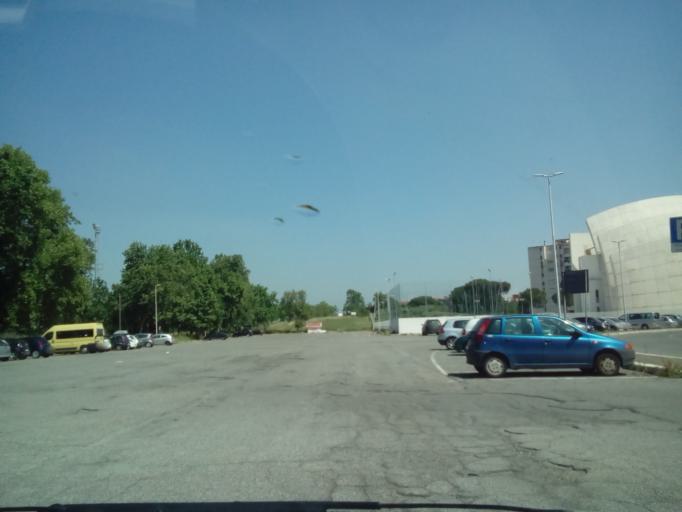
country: IT
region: Latium
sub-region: Citta metropolitana di Roma Capitale
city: Rome
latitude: 41.8811
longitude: 12.5847
